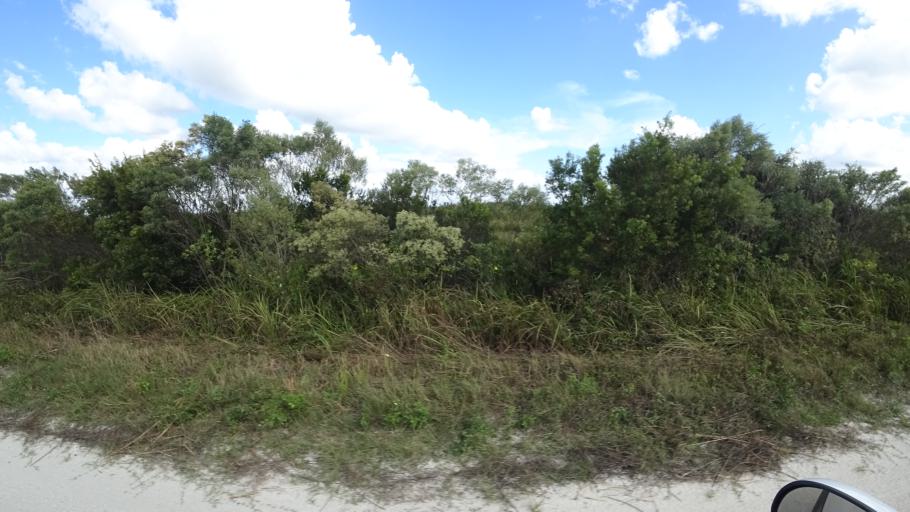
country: US
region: Florida
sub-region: DeSoto County
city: Arcadia
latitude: 27.3251
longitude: -82.1050
